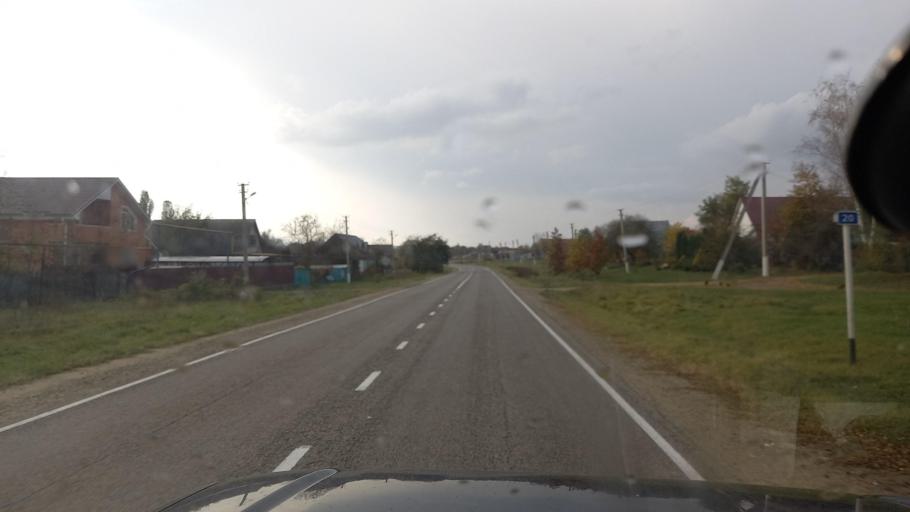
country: RU
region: Krasnodarskiy
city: Gubskaya
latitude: 44.3192
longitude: 40.6108
